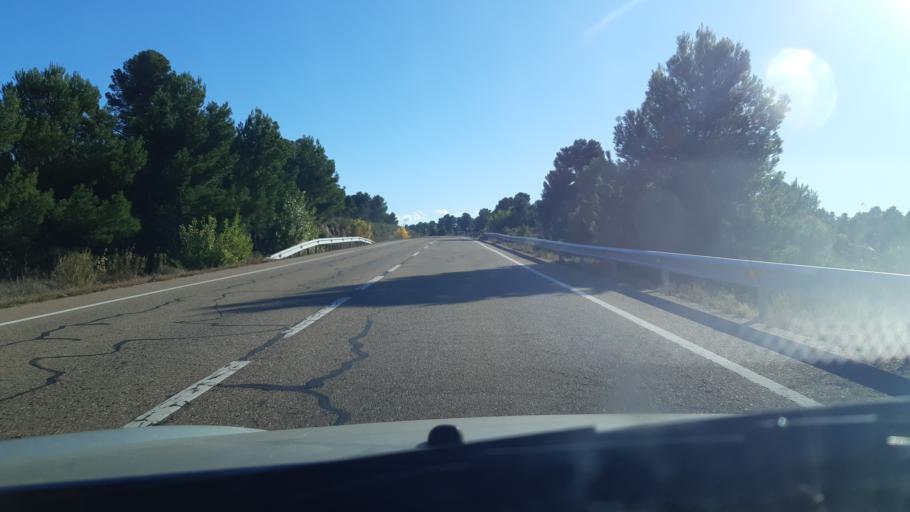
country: ES
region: Aragon
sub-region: Provincia de Teruel
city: Valjunquera
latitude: 40.9358
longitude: -0.0119
